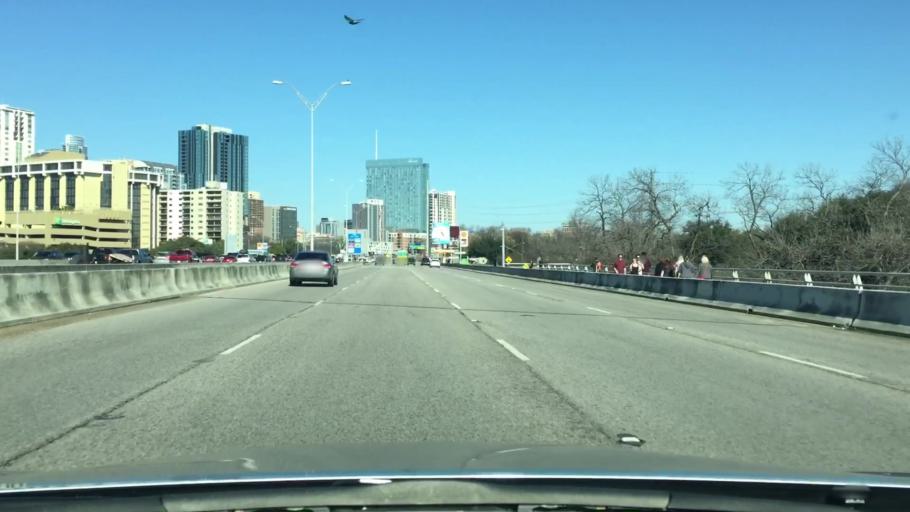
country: US
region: Texas
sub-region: Travis County
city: Austin
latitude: 30.2508
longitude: -97.7356
